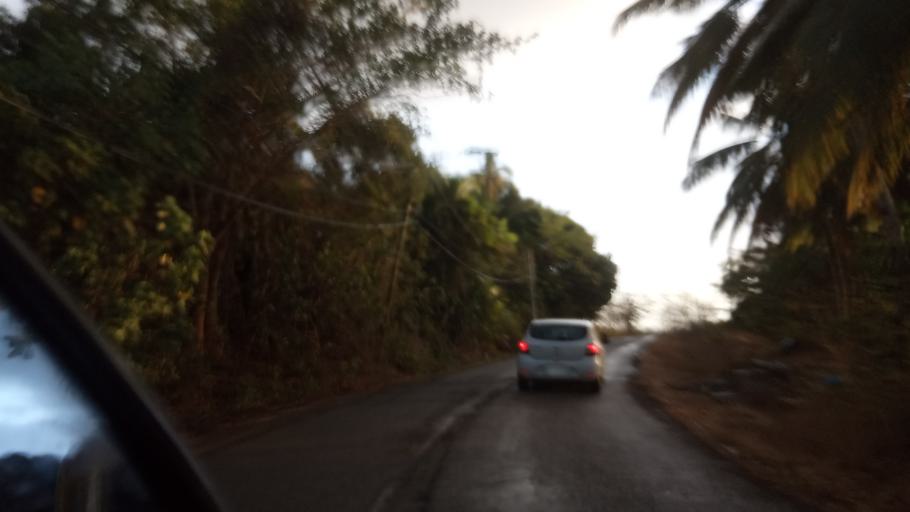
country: YT
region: Kani-Keli
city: Kani Keli
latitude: -12.9330
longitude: 45.1046
